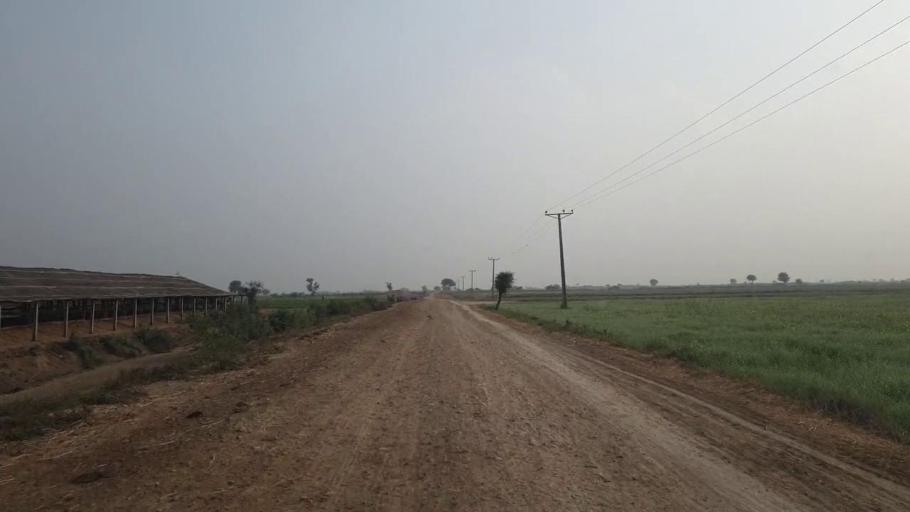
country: PK
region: Sindh
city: Mirpur Batoro
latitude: 24.5511
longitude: 68.4207
